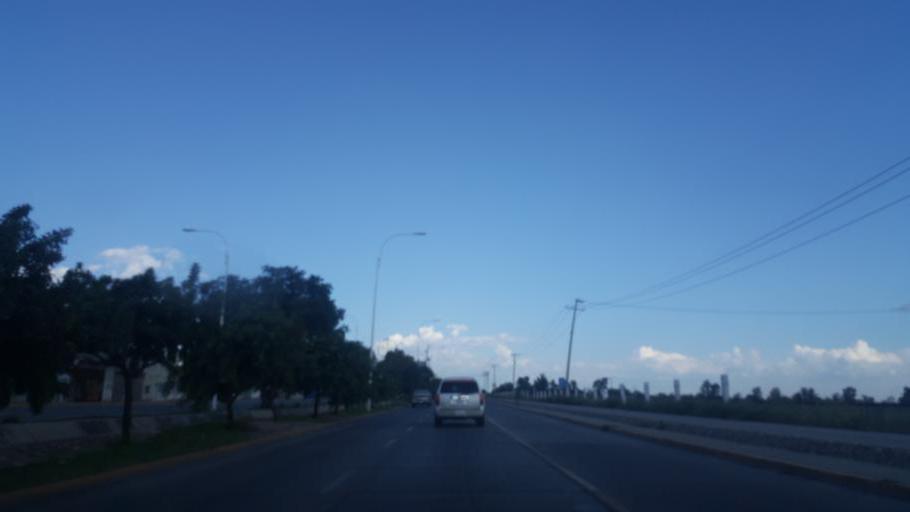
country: MX
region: Guanajuato
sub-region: Leon
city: San Jose de Duran (Los Troncoso)
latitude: 21.0787
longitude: -101.6563
